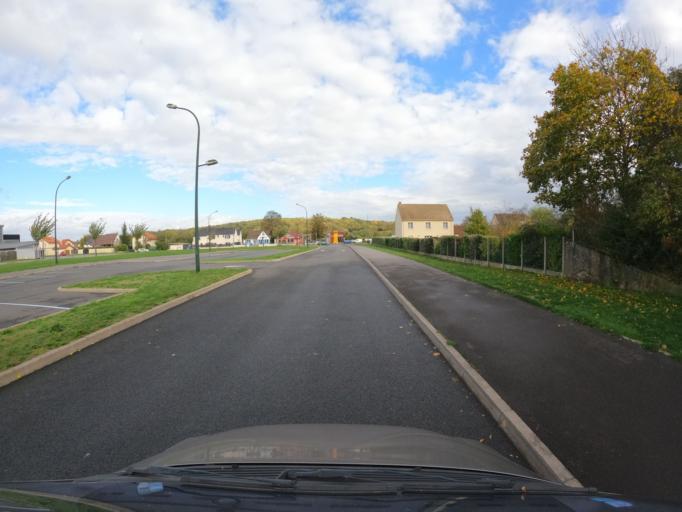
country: FR
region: Ile-de-France
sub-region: Departement de Seine-et-Marne
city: Saint-Germain-sur-Morin
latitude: 48.8827
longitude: 2.8447
